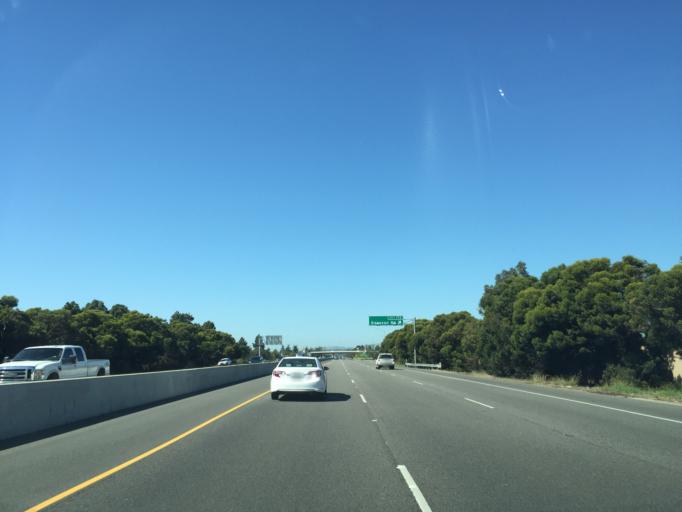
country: US
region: California
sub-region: Santa Barbara County
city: Santa Maria
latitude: 34.9623
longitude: -120.4196
